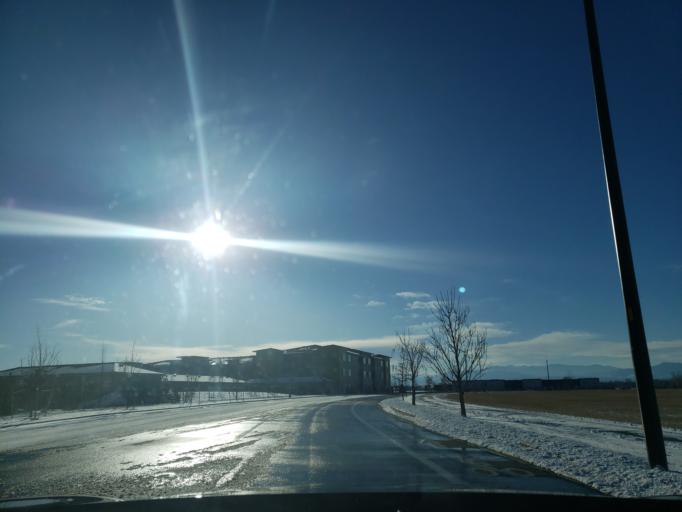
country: US
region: Colorado
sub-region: Larimer County
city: Fort Collins
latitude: 40.5194
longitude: -105.0089
